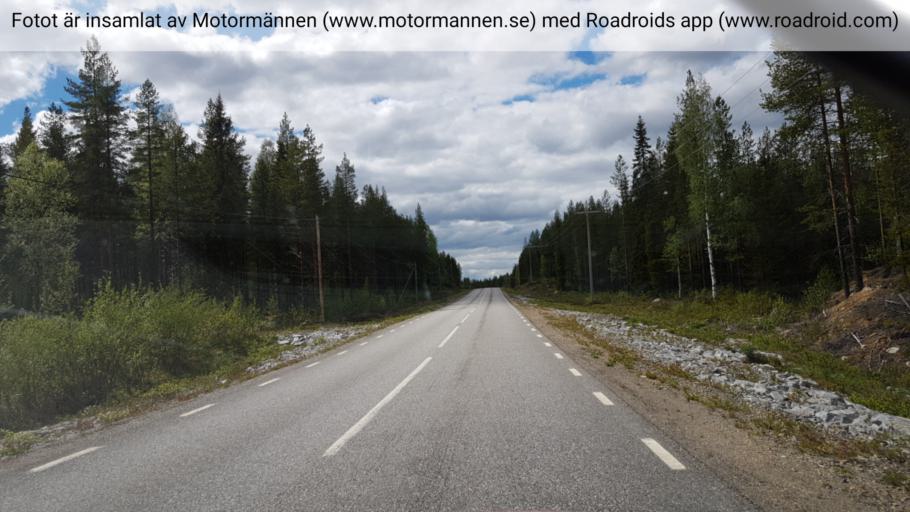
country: SE
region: Vaesterbotten
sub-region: Skelleftea Kommun
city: Langsele
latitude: 64.7642
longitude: 19.9847
